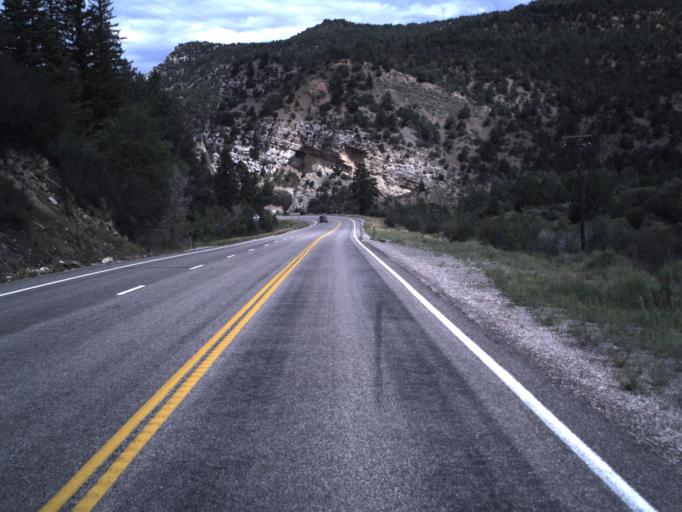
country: US
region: Utah
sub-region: Iron County
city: Cedar City
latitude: 37.6381
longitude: -112.9510
